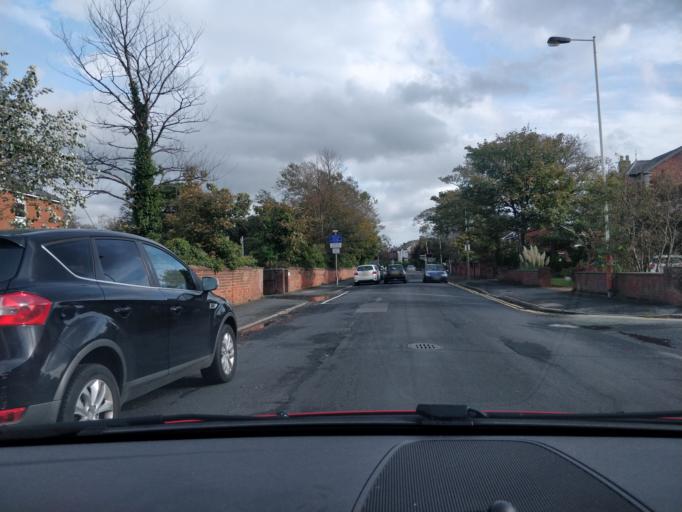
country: GB
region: England
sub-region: Sefton
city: Southport
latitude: 53.6299
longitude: -3.0200
